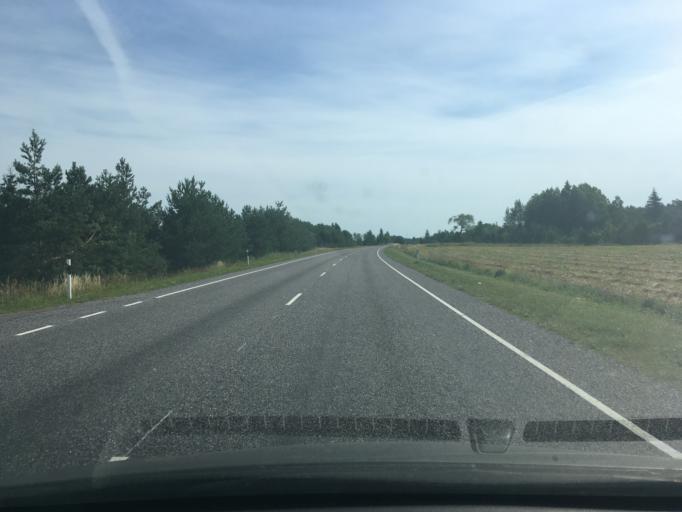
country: EE
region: Laeaene
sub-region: Lihula vald
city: Lihula
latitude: 58.6667
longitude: 23.7445
